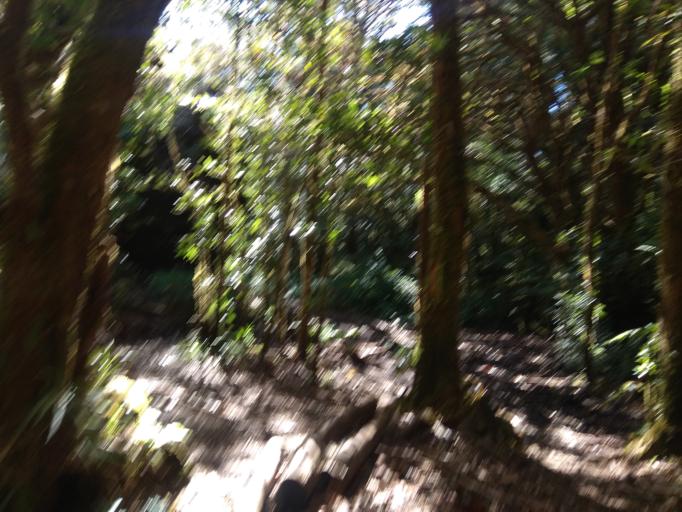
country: CR
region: Heredia
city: Santo Domingo
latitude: 10.1326
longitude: -84.1175
